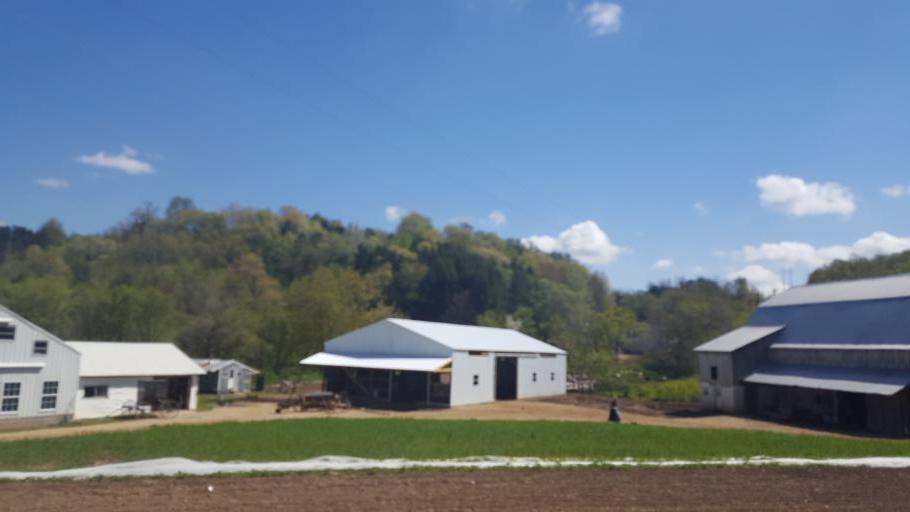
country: US
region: Wisconsin
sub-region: Vernon County
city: Hillsboro
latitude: 43.5937
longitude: -90.3640
